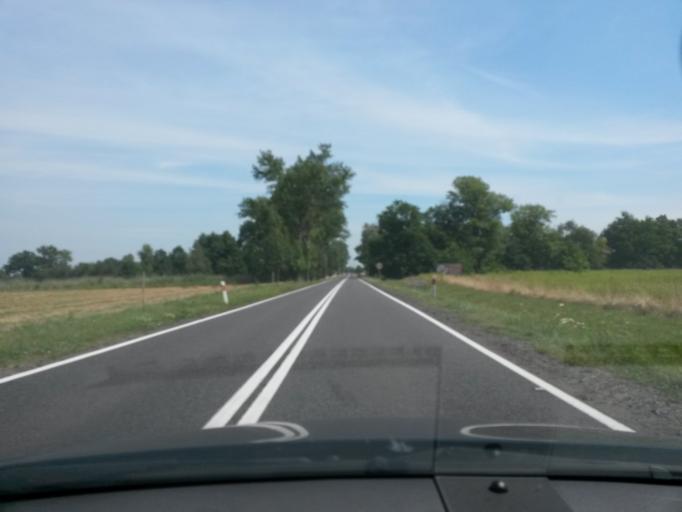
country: PL
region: Lower Silesian Voivodeship
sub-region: Powiat lubinski
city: Scinawa
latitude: 51.4136
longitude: 16.4502
